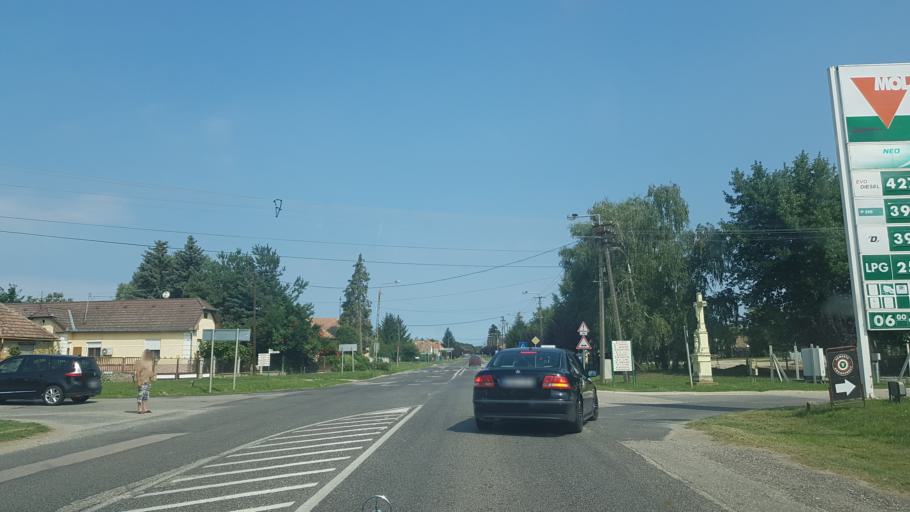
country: HU
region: Somogy
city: Segesd
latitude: 46.3421
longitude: 17.3479
